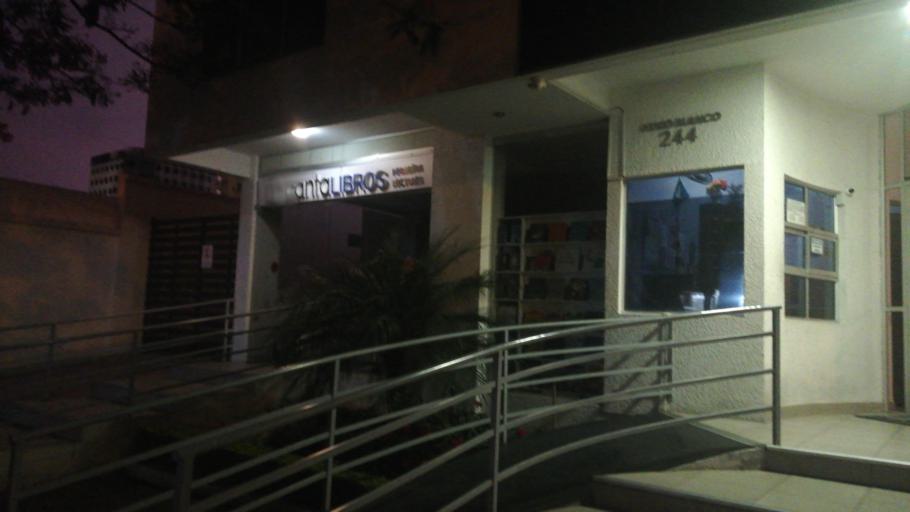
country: BO
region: Cochabamba
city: Cochabamba
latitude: -17.3762
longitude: -66.1583
